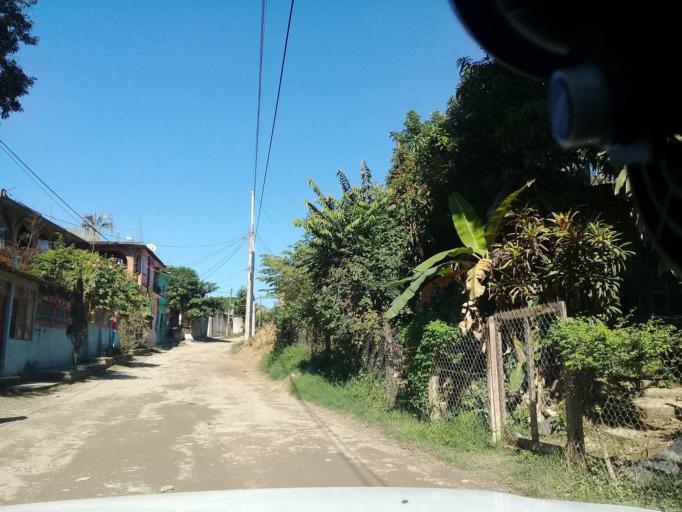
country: MX
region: Hidalgo
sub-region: Huejutla de Reyes
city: Huejutla de Reyes
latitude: 21.1620
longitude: -98.4172
